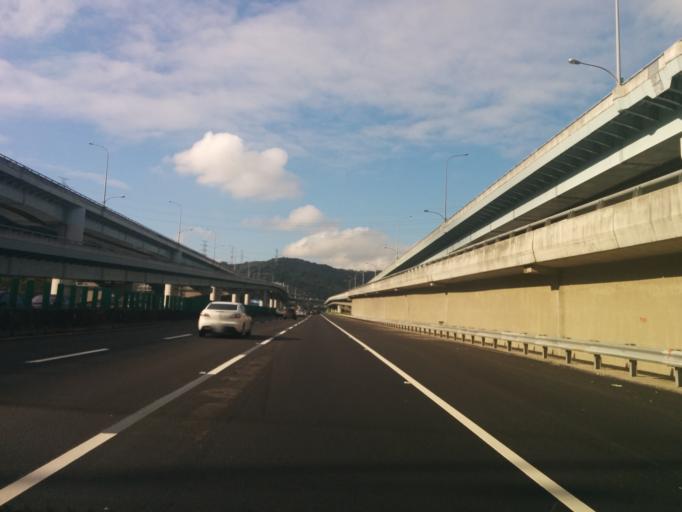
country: TW
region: Taipei
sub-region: Taipei
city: Banqiao
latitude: 25.0608
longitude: 121.4141
